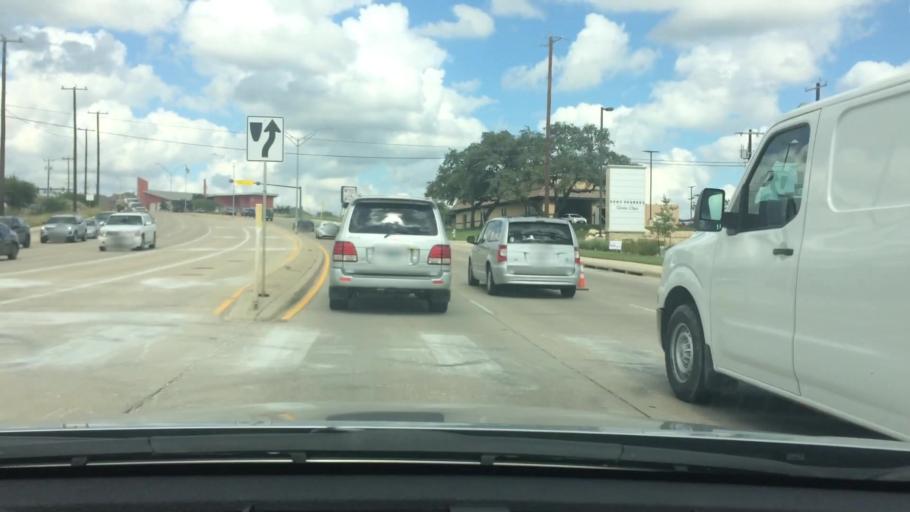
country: US
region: Texas
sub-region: Bexar County
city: Hollywood Park
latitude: 29.6050
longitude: -98.4184
